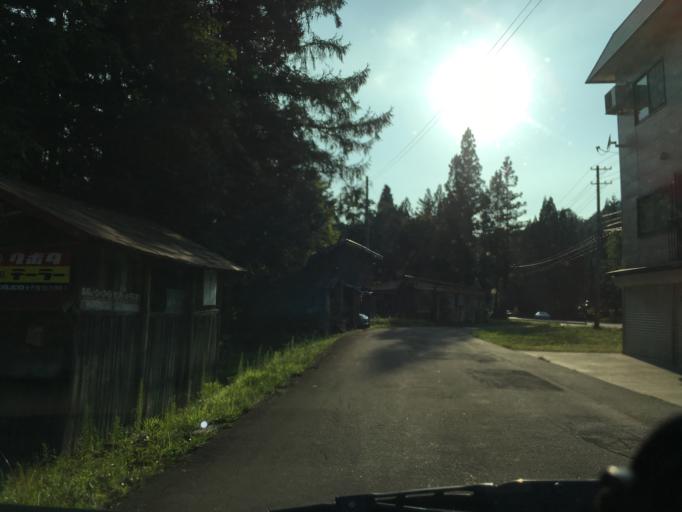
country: JP
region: Yamagata
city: Yonezawa
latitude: 37.9110
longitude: 140.0440
